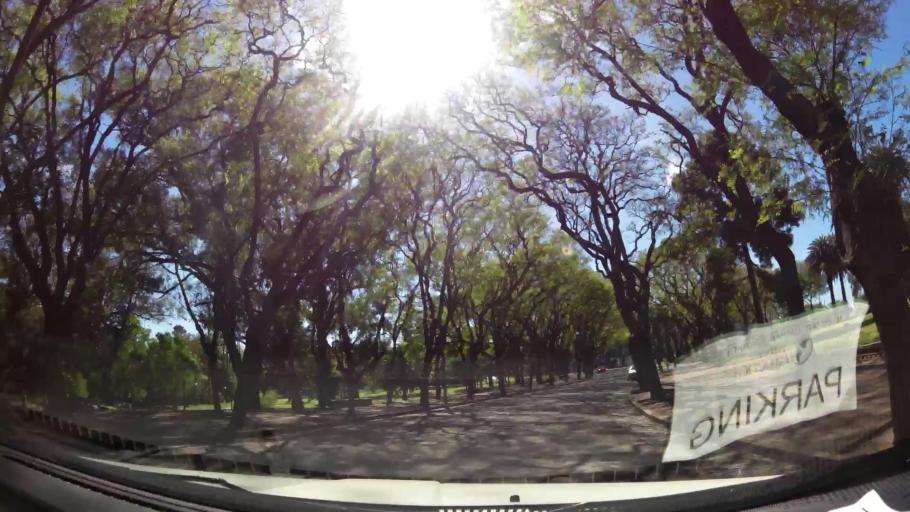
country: UY
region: Montevideo
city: Montevideo
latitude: -34.9141
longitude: -56.1676
